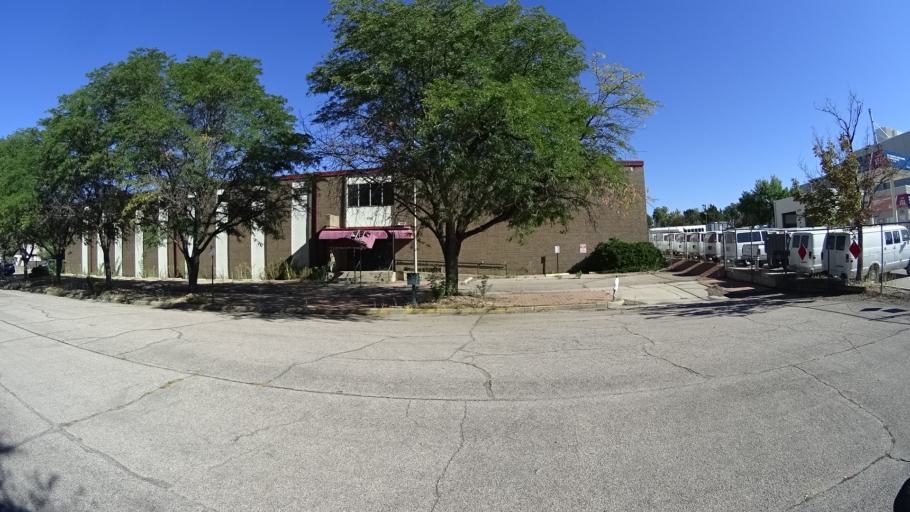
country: US
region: Colorado
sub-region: El Paso County
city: Colorado Springs
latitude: 38.8414
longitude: -104.7974
